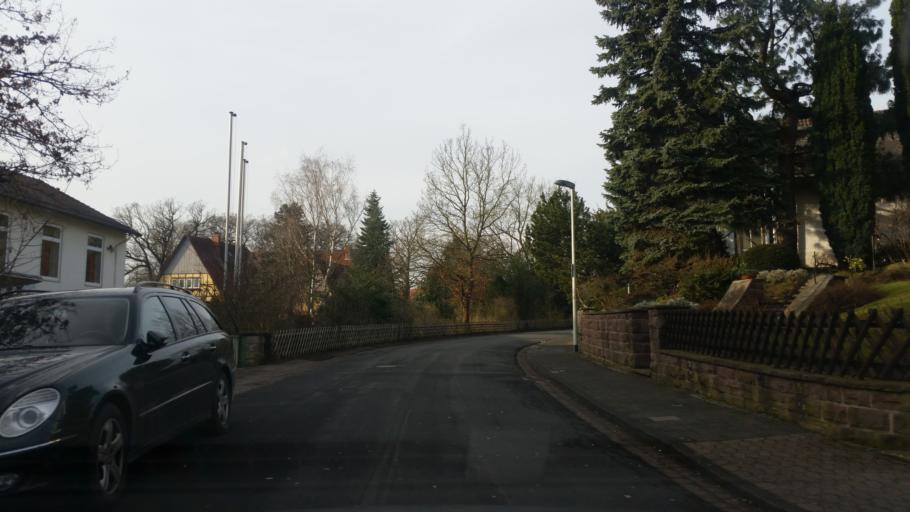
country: DE
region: Lower Saxony
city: Hameln
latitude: 52.1188
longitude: 9.3620
